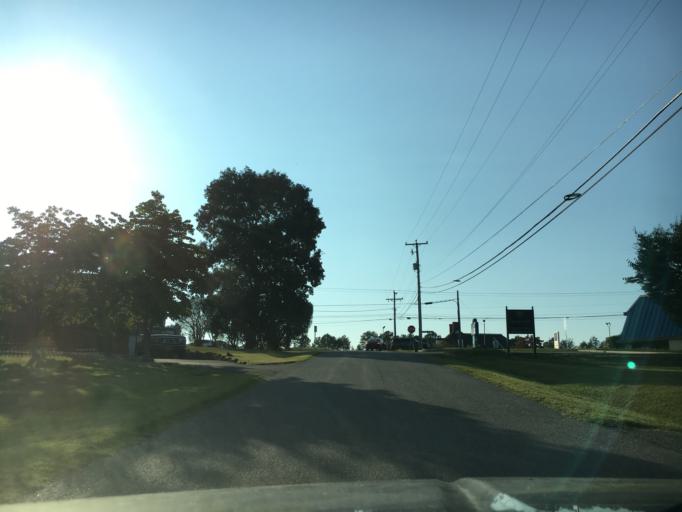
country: US
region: Virginia
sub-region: Campbell County
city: Timberlake
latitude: 37.3421
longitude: -79.2349
